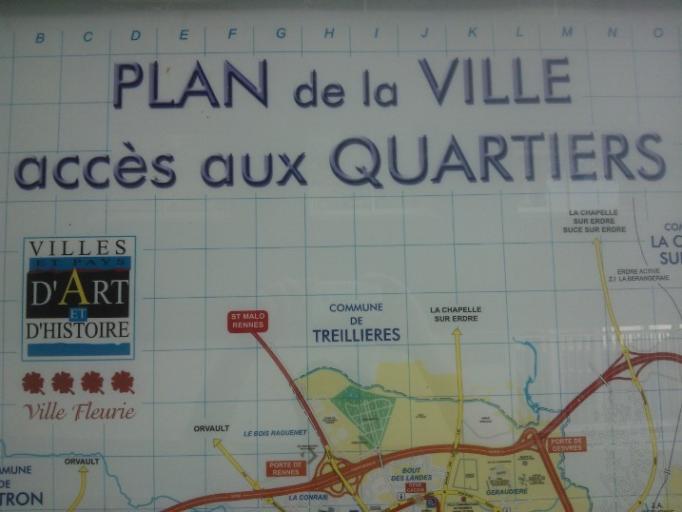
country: FR
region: Pays de la Loire
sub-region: Departement de la Loire-Atlantique
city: Nantes
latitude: 47.2016
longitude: -1.5778
